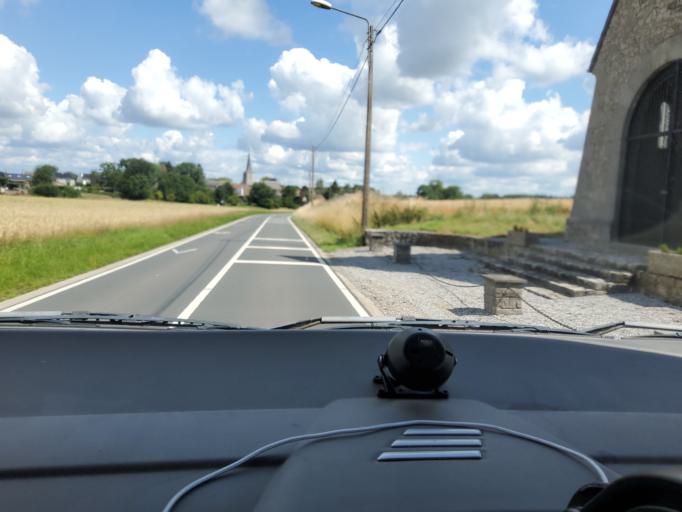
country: BE
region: Wallonia
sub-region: Province du Hainaut
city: Fleurus
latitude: 50.5004
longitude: 4.5498
